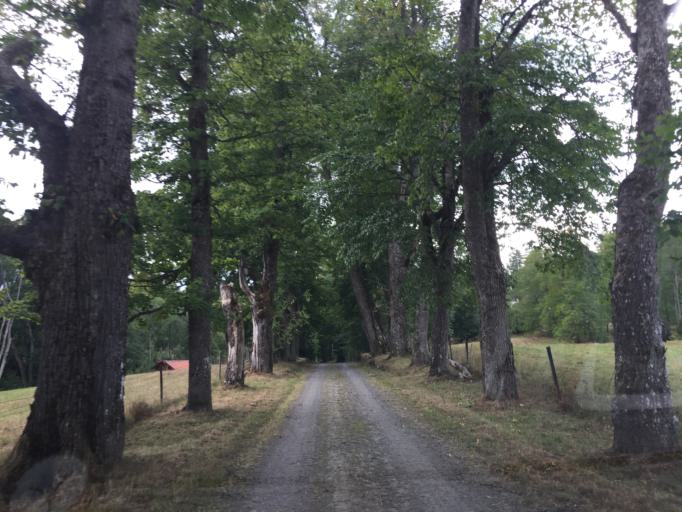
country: SE
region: Vaermland
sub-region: Filipstads Kommun
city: Lesjofors
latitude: 60.0259
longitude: 14.1092
